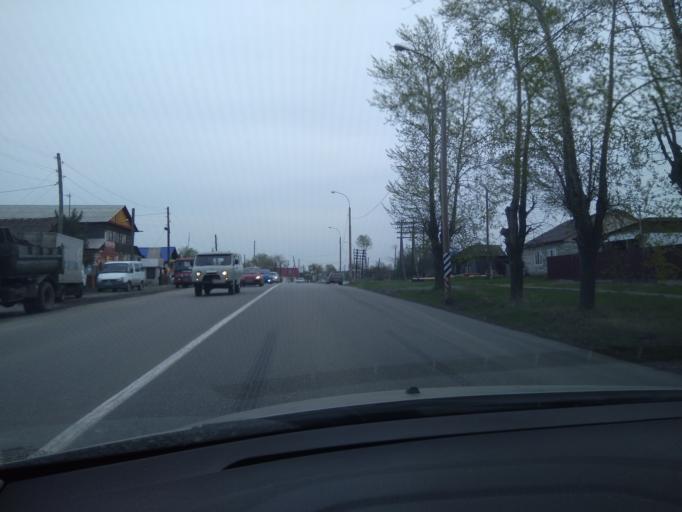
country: RU
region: Sverdlovsk
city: Beloyarskiy
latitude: 56.7570
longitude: 61.3717
